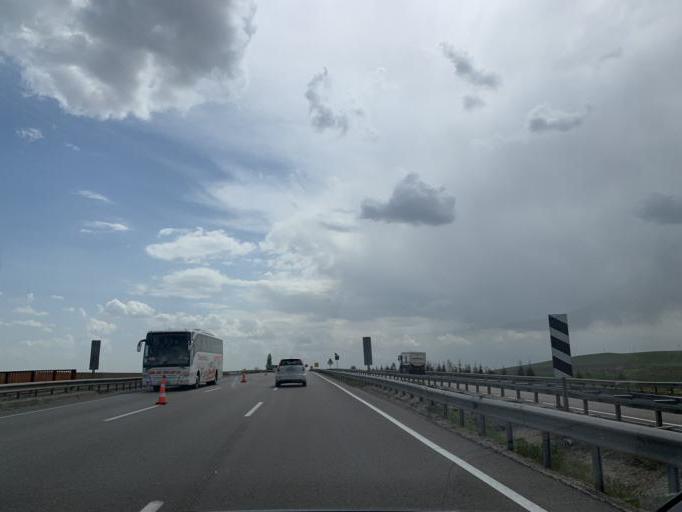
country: TR
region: Ankara
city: Polatli
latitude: 39.6189
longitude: 32.1890
